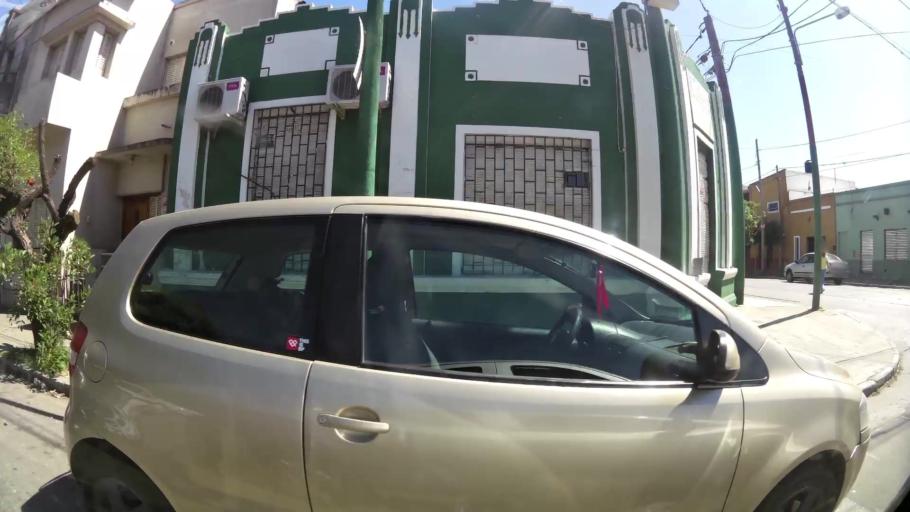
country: AR
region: Cordoba
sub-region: Departamento de Capital
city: Cordoba
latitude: -31.4228
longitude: -64.1418
